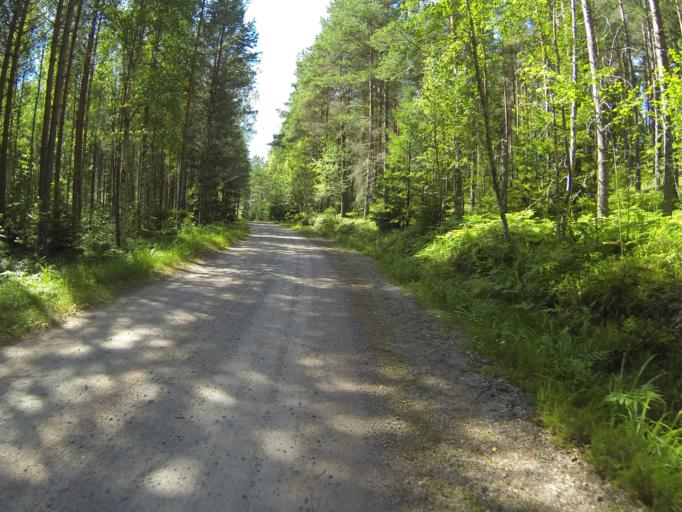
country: FI
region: Varsinais-Suomi
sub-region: Salo
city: Pernioe
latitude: 60.2874
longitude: 23.0772
